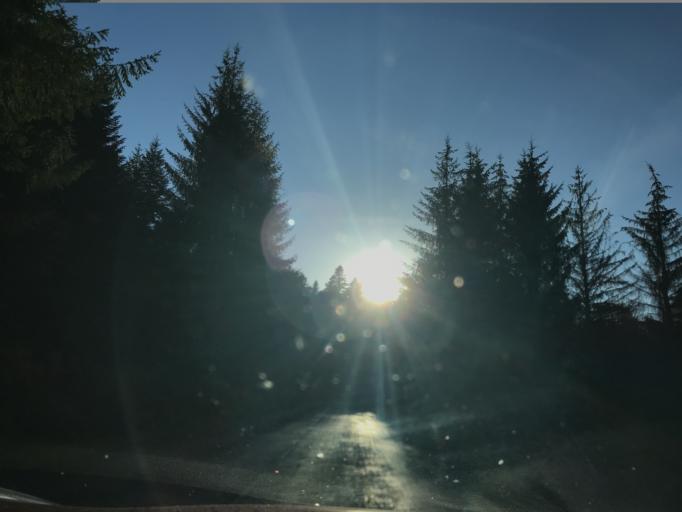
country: FR
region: Rhone-Alpes
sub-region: Departement de la Loire
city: Noiretable
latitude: 45.7984
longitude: 3.7113
